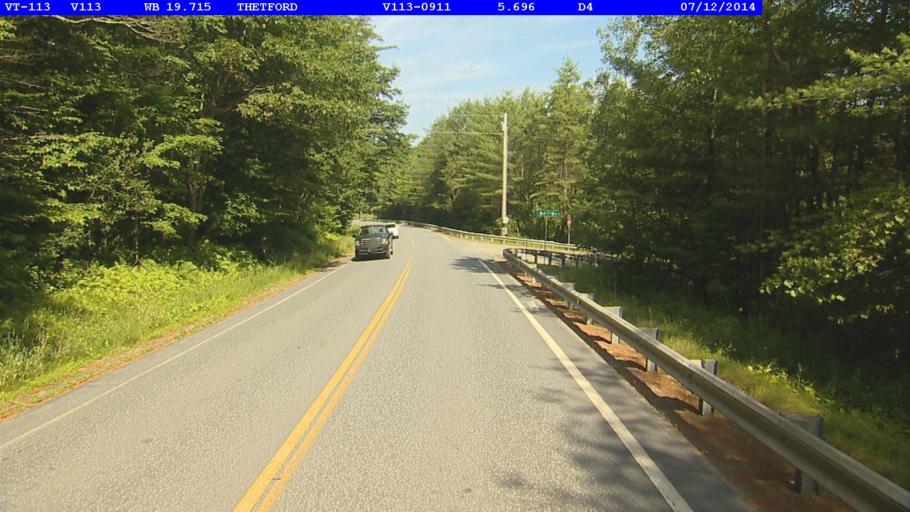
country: US
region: New Hampshire
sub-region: Grafton County
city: Lyme
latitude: 43.8247
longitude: -72.2359
